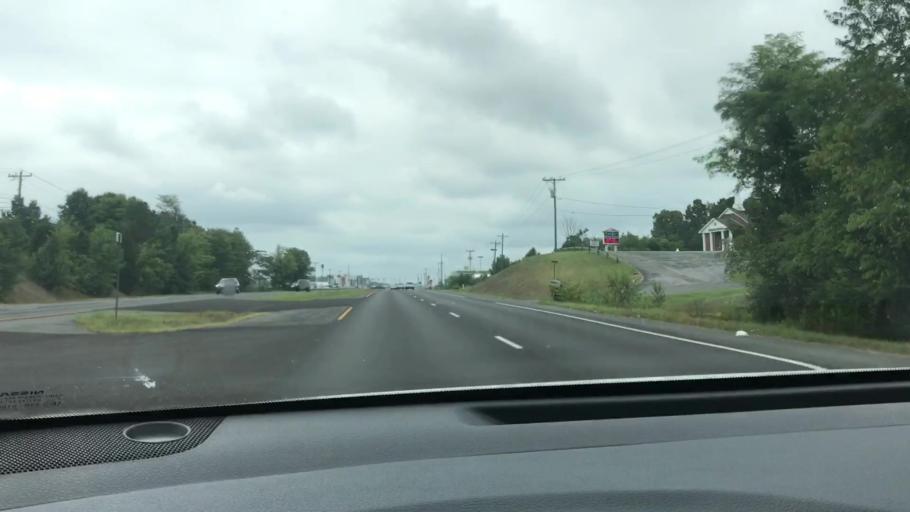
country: US
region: Kentucky
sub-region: Calloway County
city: Murray
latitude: 36.6446
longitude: -88.3084
